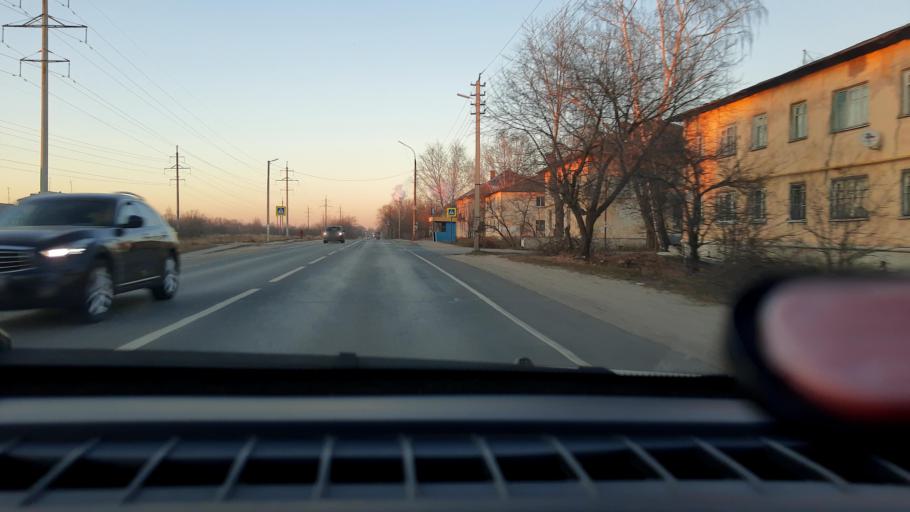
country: RU
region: Nizjnij Novgorod
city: Novaya Balakhna
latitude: 56.4795
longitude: 43.6045
